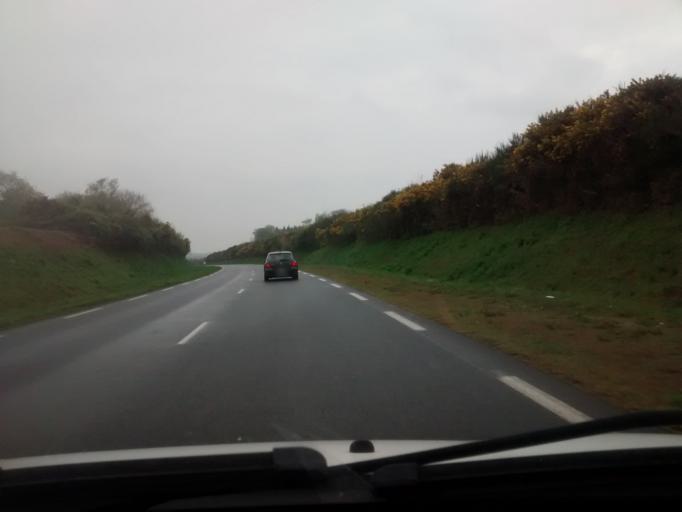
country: FR
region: Brittany
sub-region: Departement des Cotes-d'Armor
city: Saint-Quay-Perros
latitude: 48.7598
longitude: -3.4470
